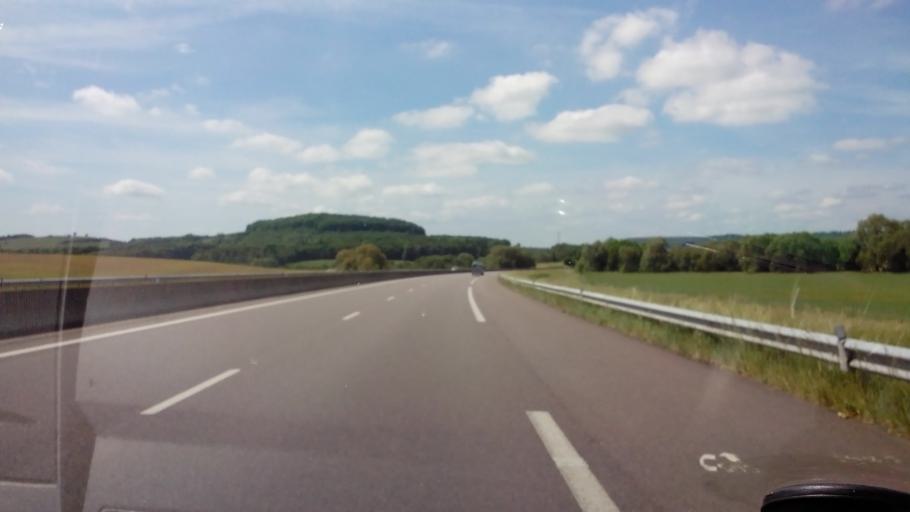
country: FR
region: Lorraine
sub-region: Departement des Vosges
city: Chatenois
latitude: 48.3577
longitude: 5.8654
